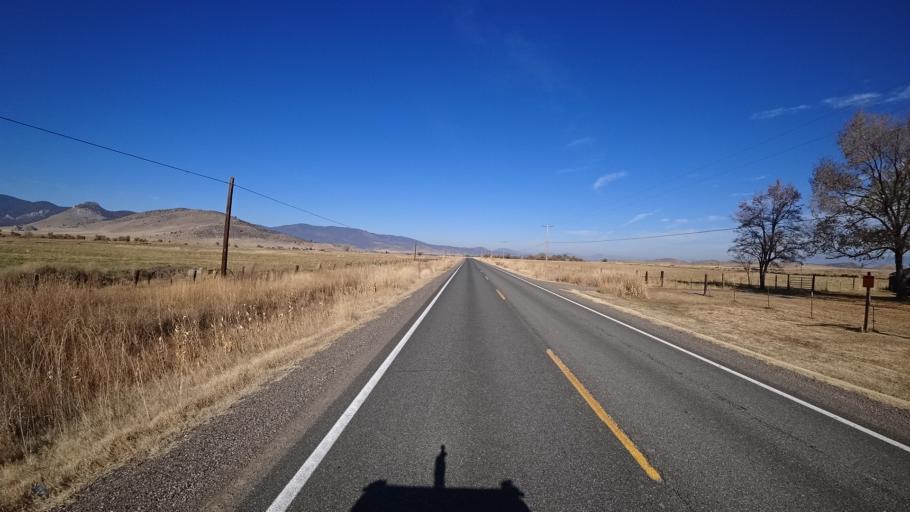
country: US
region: California
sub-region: Siskiyou County
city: Weed
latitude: 41.5012
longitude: -122.5145
